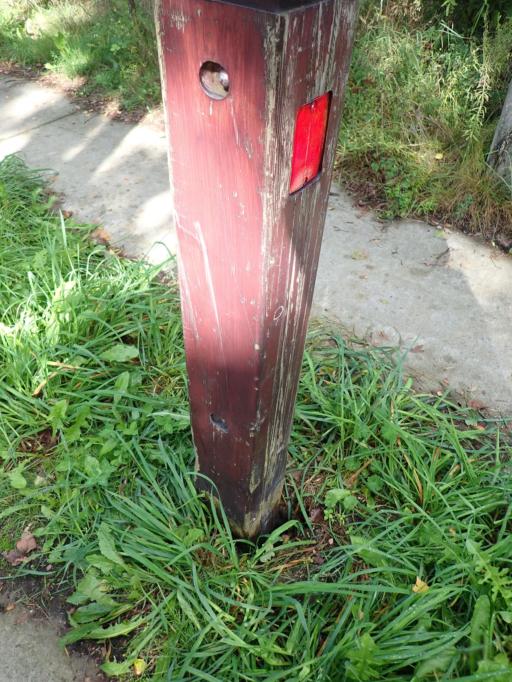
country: BE
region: Flanders
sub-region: Provincie Antwerpen
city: Hulshout
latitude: 51.0891
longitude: 4.8067
